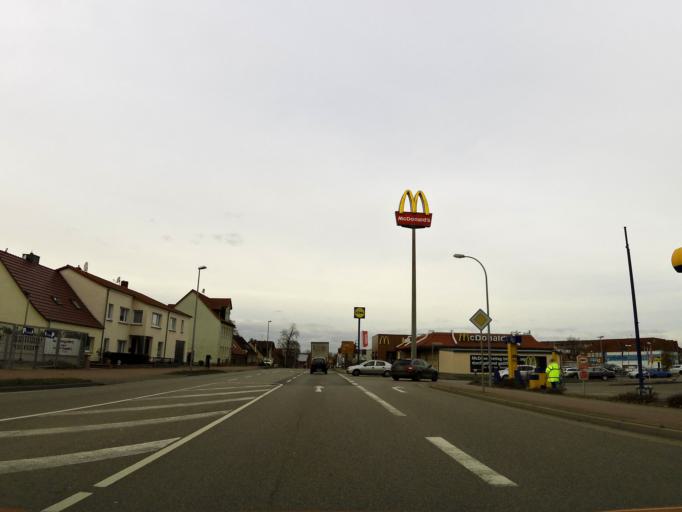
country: DE
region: Saxony-Anhalt
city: Salzwedel
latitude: 52.8405
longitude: 11.1723
